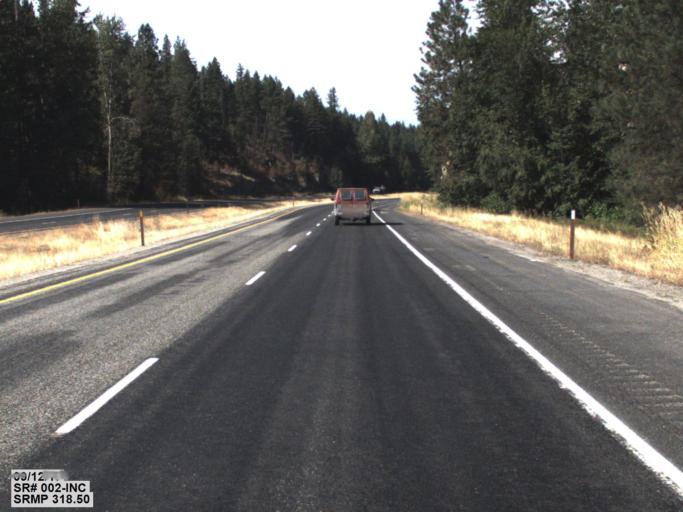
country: US
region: Washington
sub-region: Spokane County
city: Deer Park
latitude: 48.0850
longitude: -117.3247
